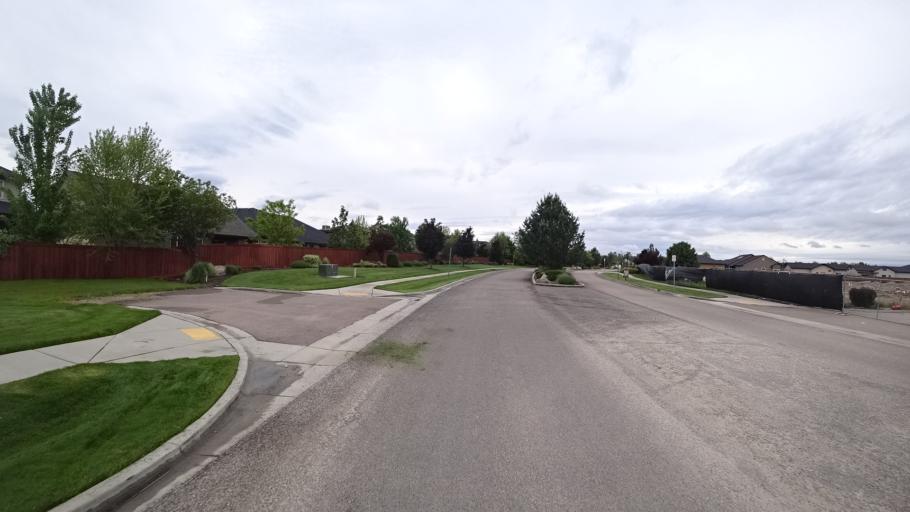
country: US
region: Idaho
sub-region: Ada County
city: Star
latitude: 43.6906
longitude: -116.4731
